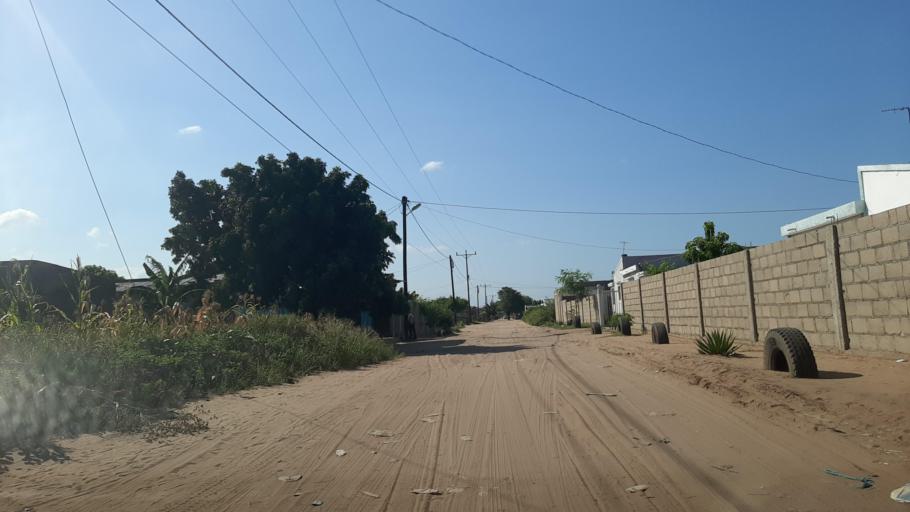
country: MZ
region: Maputo
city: Matola
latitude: -25.8086
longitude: 32.4919
